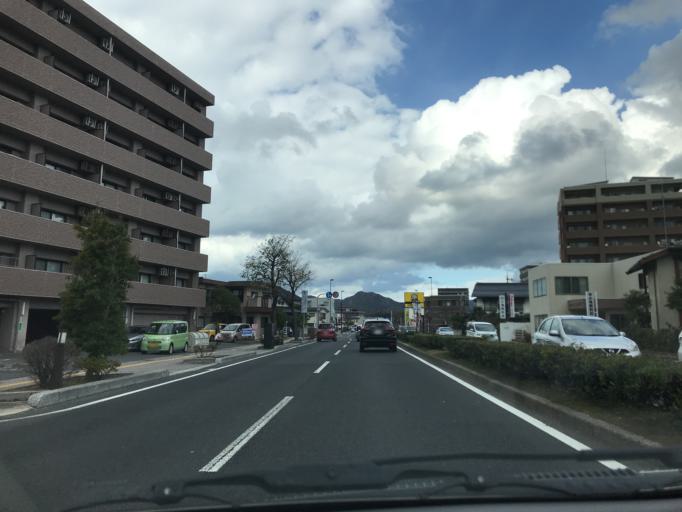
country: JP
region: Shimane
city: Matsue-shi
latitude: 35.4742
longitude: 133.0642
